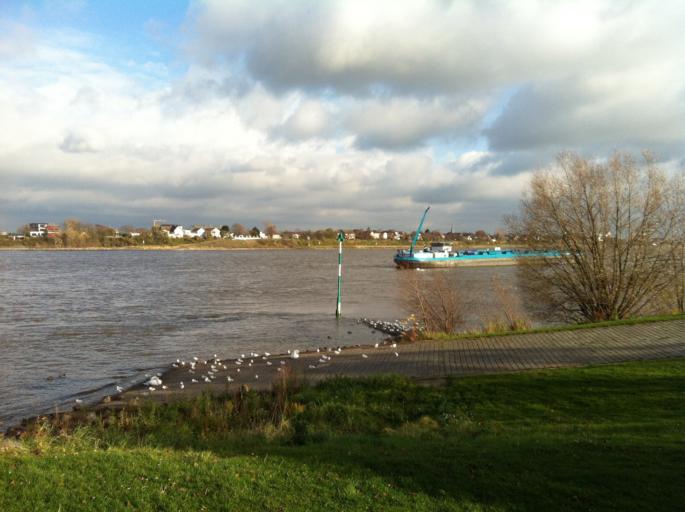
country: DE
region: North Rhine-Westphalia
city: Wesseling
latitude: 50.8249
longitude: 6.9872
